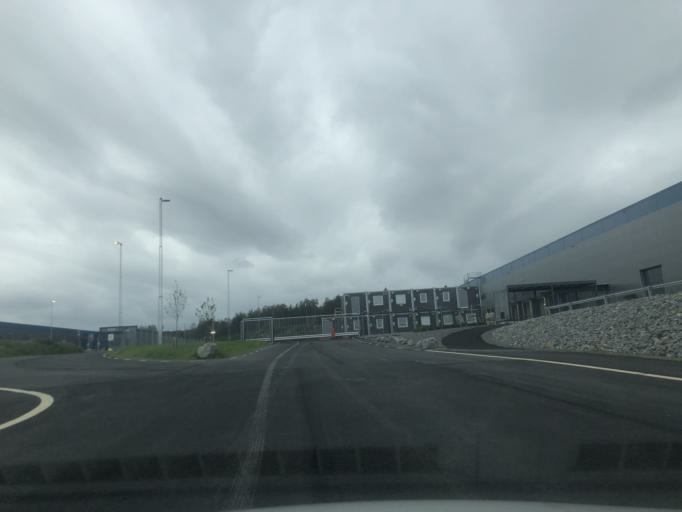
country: SE
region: Vaestra Goetaland
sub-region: Goteborg
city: Majorna
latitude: 57.7360
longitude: 11.8684
